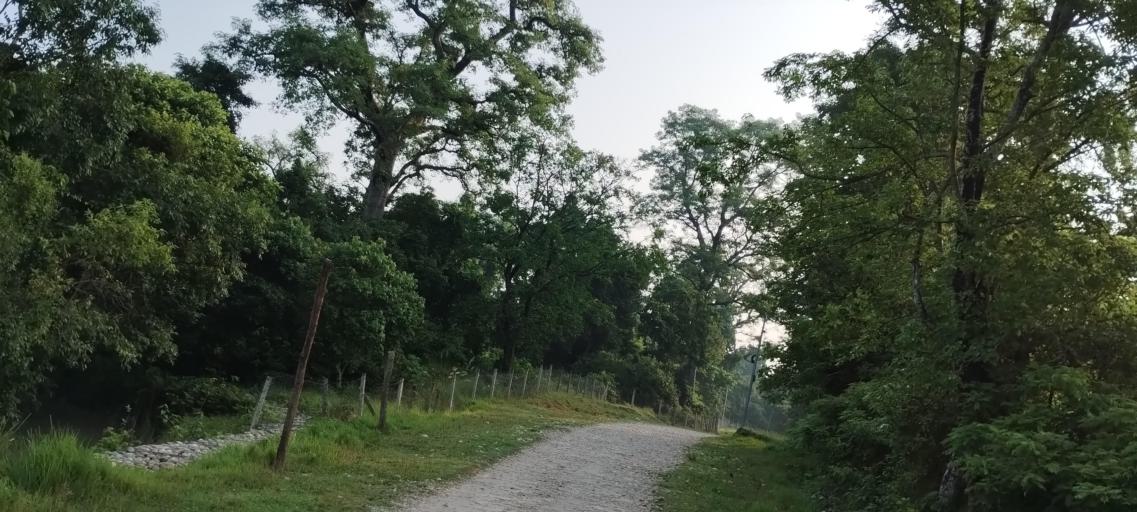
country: NP
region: Far Western
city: Tikapur
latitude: 28.4504
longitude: 81.2397
